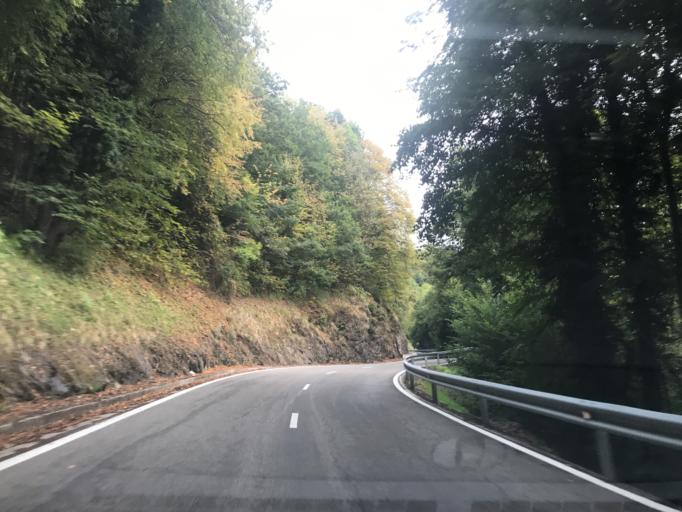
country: ES
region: Catalonia
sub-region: Provincia de Lleida
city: Les
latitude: 42.7739
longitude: 0.6807
